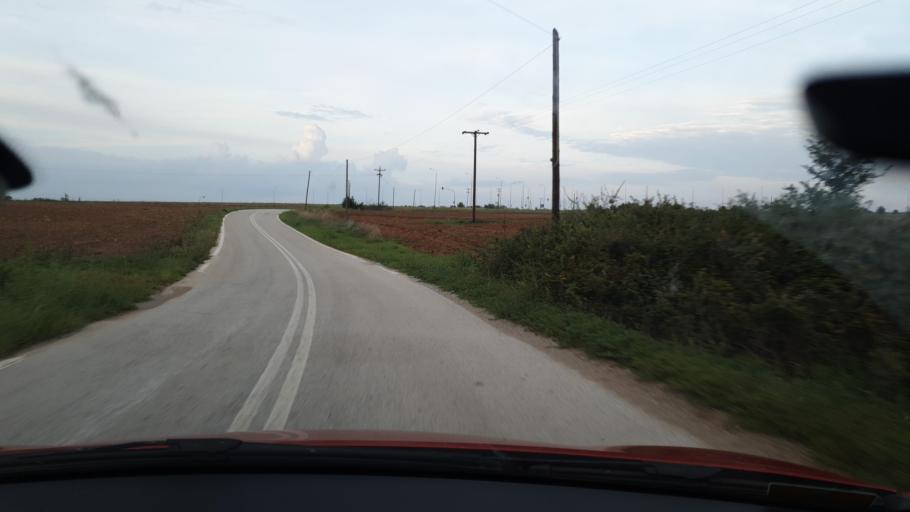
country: GR
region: Central Macedonia
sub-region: Nomos Kilkis
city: Kristoni
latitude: 40.9512
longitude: 22.8266
